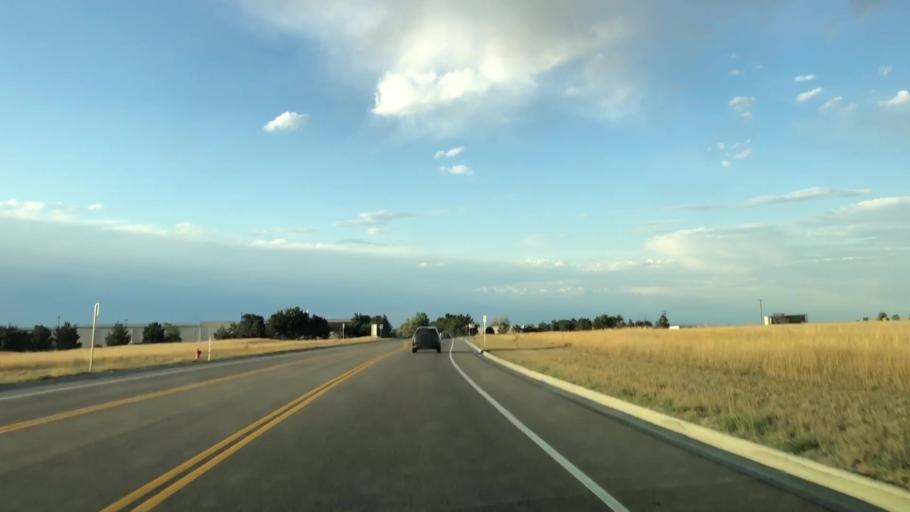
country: US
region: Colorado
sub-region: Larimer County
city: Loveland
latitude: 40.4469
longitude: -104.9945
